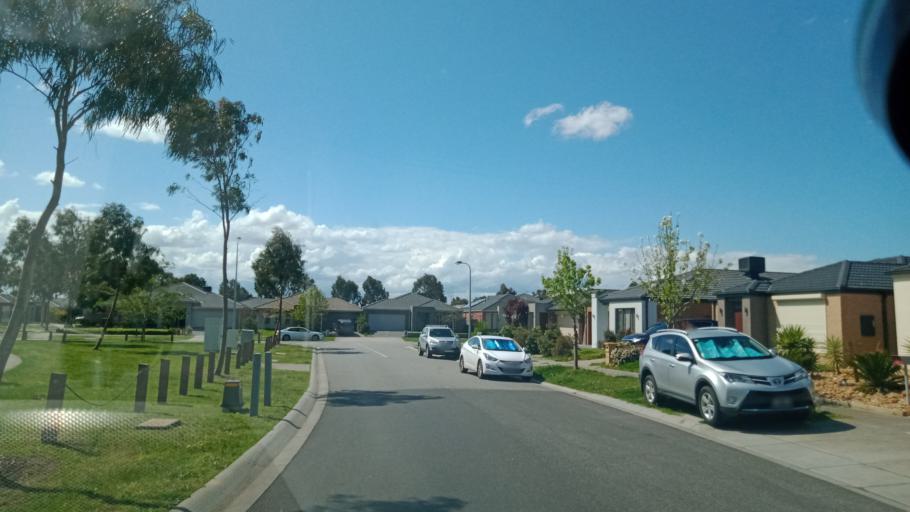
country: AU
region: Victoria
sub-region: Casey
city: Cranbourne West
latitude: -38.0987
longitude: 145.2526
